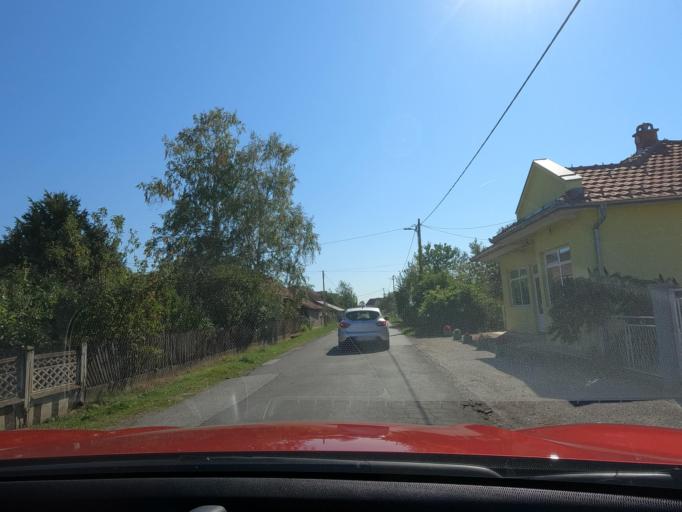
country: RS
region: Central Serbia
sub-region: Raski Okrug
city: Kraljevo
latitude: 43.7468
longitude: 20.7188
